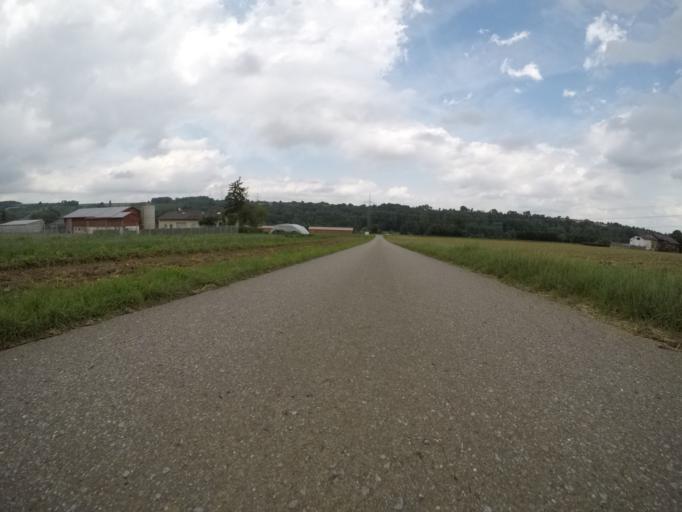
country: DE
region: Baden-Wuerttemberg
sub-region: Regierungsbezirk Stuttgart
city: Oberriexingen
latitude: 48.9214
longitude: 9.0084
